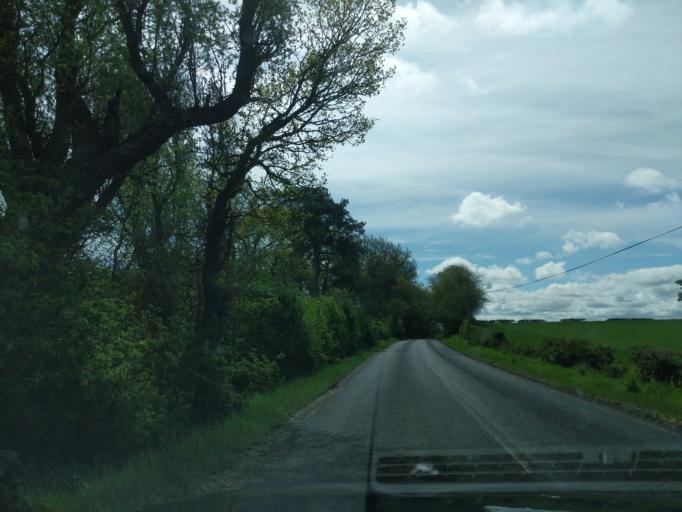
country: GB
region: Scotland
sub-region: The Scottish Borders
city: Saint Boswells
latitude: 55.6311
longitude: -2.5806
